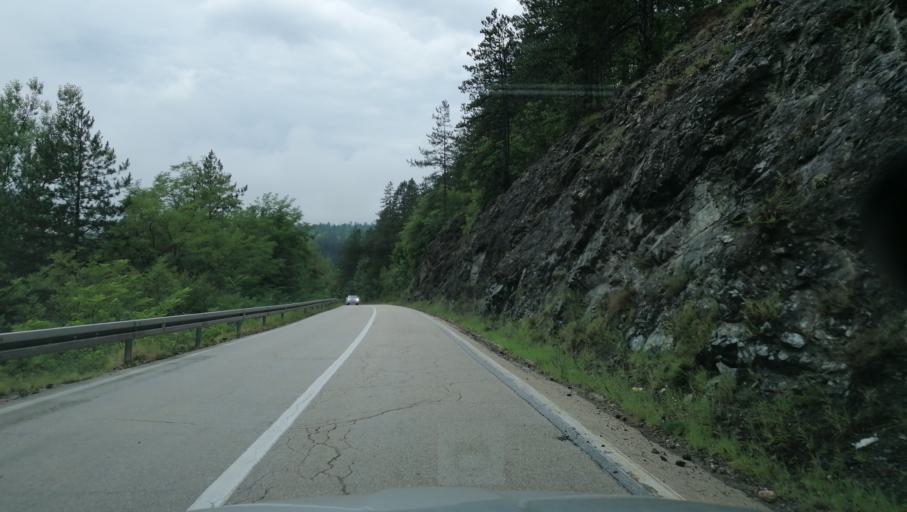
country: BA
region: Republika Srpska
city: Visegrad
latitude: 43.7860
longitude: 19.3365
